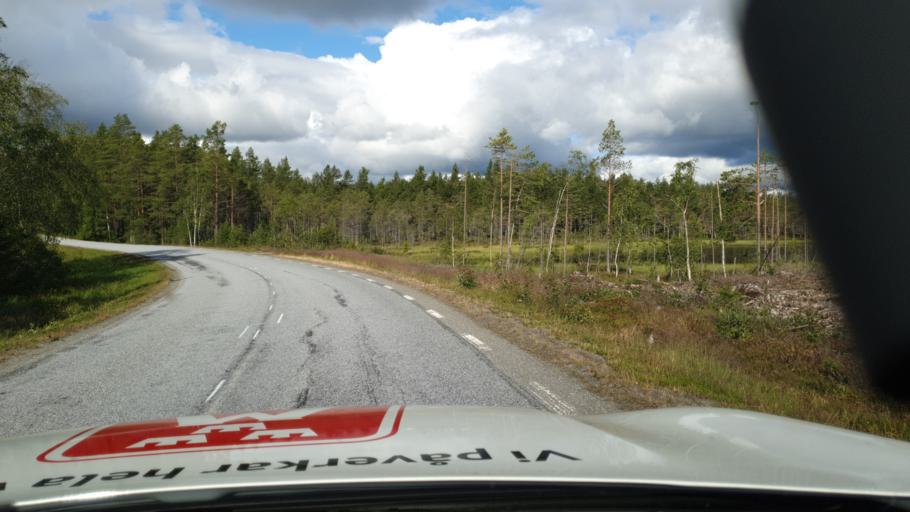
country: SE
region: Vaesterbotten
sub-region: Umea Kommun
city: Roback
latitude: 63.6755
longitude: 20.1054
